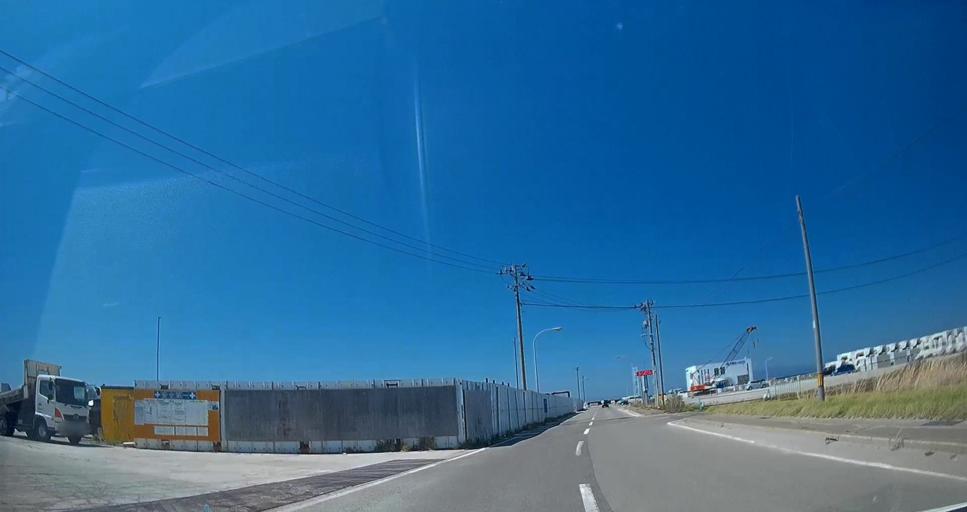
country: JP
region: Hokkaido
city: Hakodate
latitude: 41.5245
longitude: 140.8996
